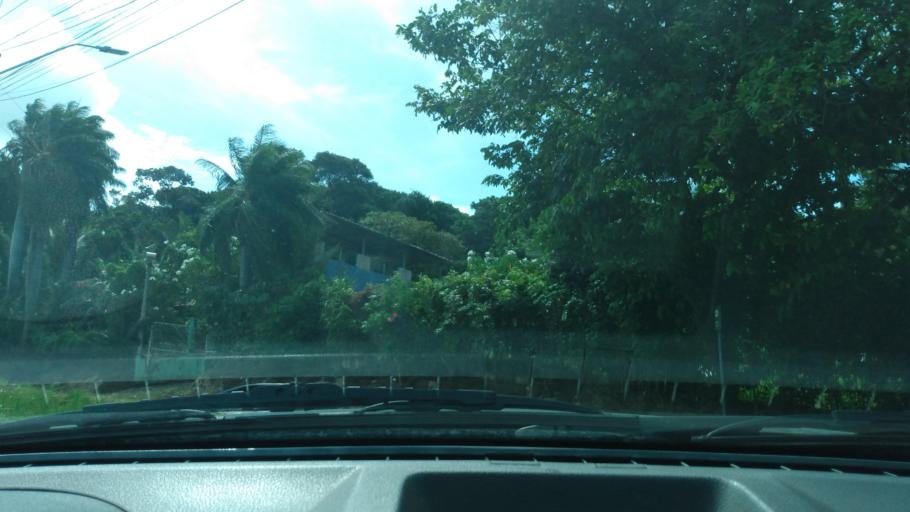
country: BR
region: Pernambuco
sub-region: Cabo De Santo Agostinho
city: Cabo
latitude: -8.3448
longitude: -34.9627
